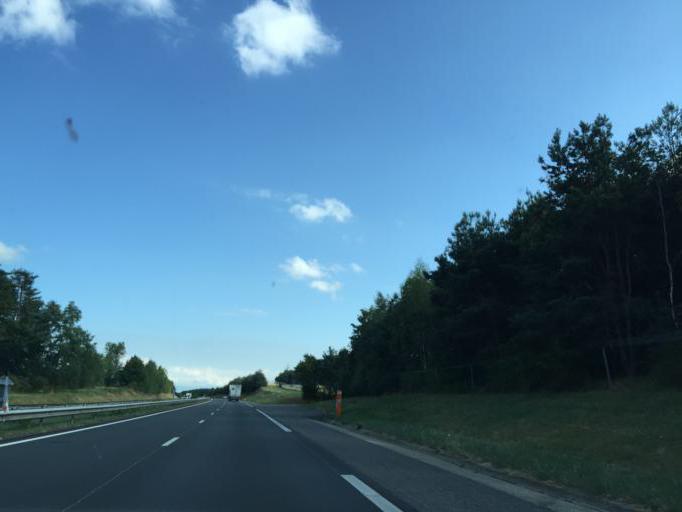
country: FR
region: Rhone-Alpes
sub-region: Departement de la Loire
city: Balbigny
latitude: 45.7832
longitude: 4.1423
